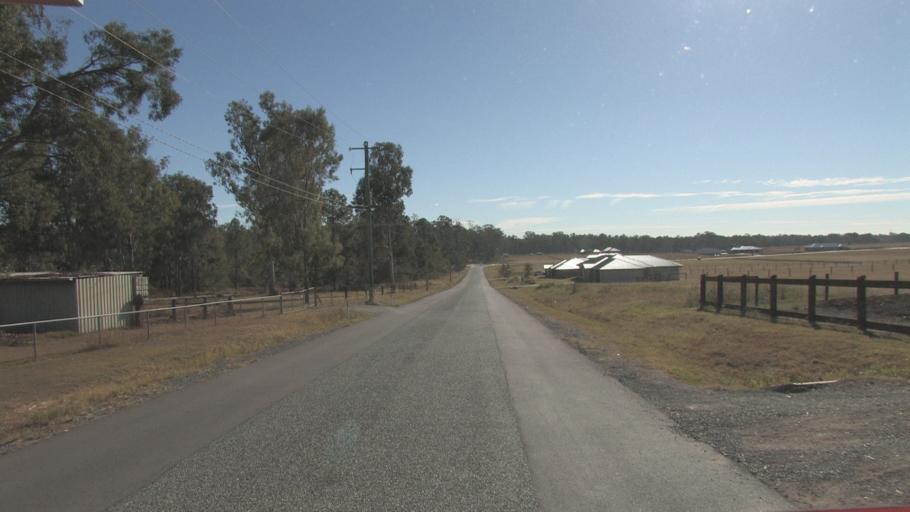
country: AU
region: Queensland
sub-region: Logan
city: North Maclean
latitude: -27.8144
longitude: 152.9921
